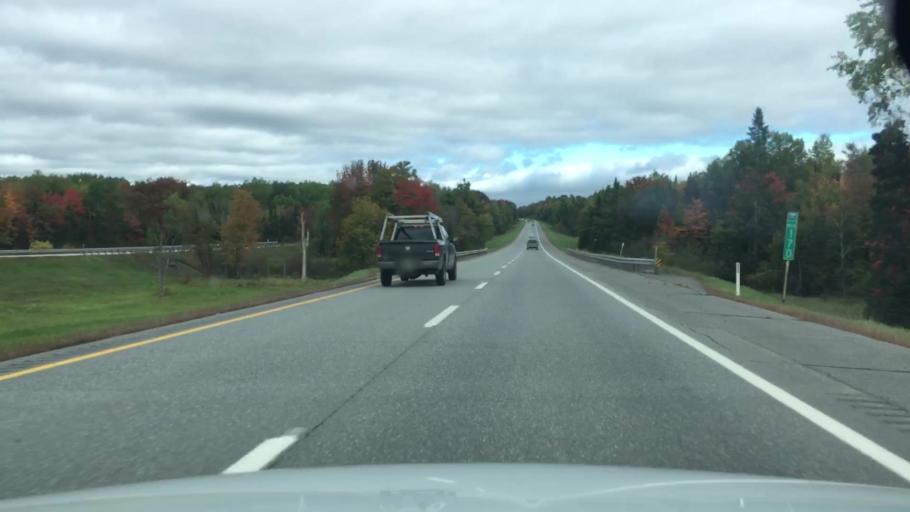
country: US
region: Maine
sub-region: Penobscot County
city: Carmel
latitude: 44.7757
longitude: -69.0451
